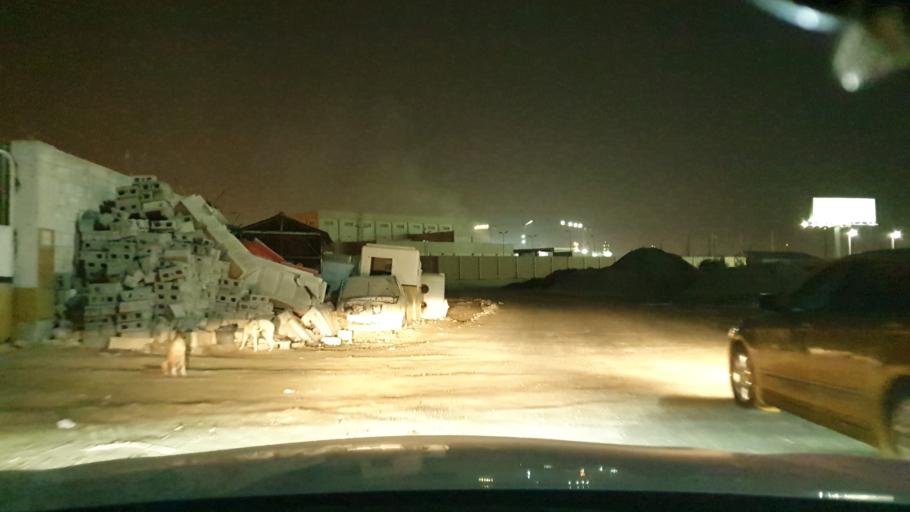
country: BH
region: Northern
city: Sitrah
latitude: 26.0952
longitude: 50.6115
